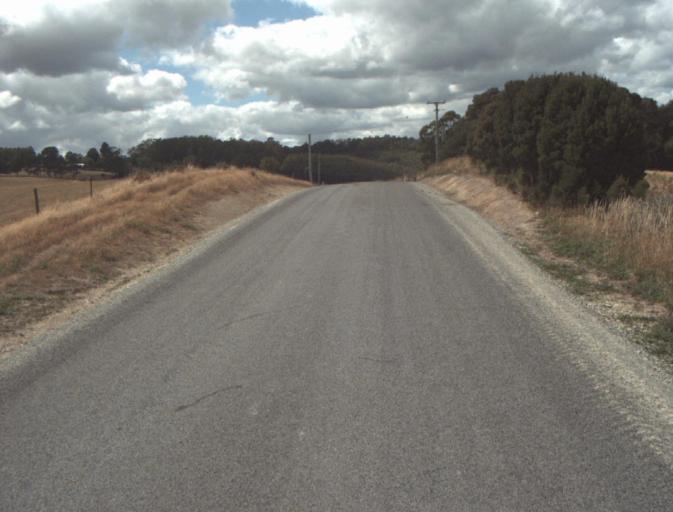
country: AU
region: Tasmania
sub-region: Launceston
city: Mayfield
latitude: -41.1933
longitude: 147.1692
